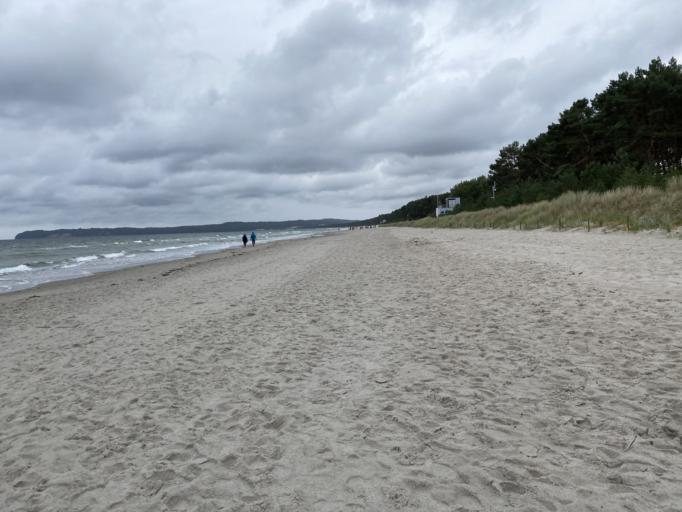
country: DE
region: Mecklenburg-Vorpommern
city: Ostseebad Binz
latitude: 54.4375
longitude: 13.5789
